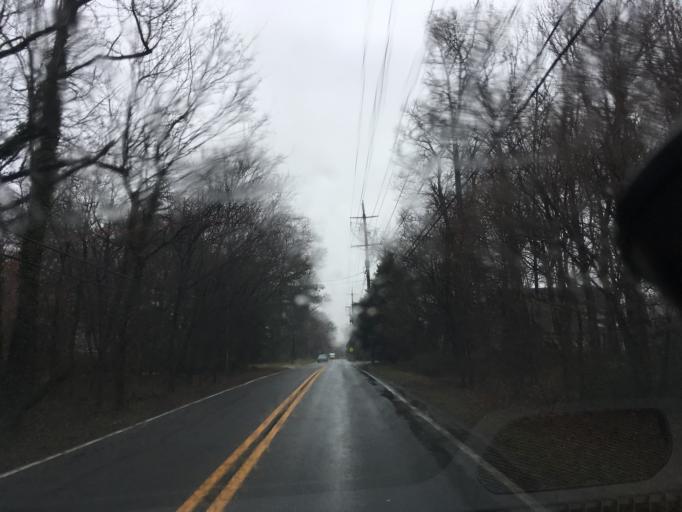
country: US
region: Delaware
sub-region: New Castle County
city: Bellefonte
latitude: 39.7865
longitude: -75.5206
